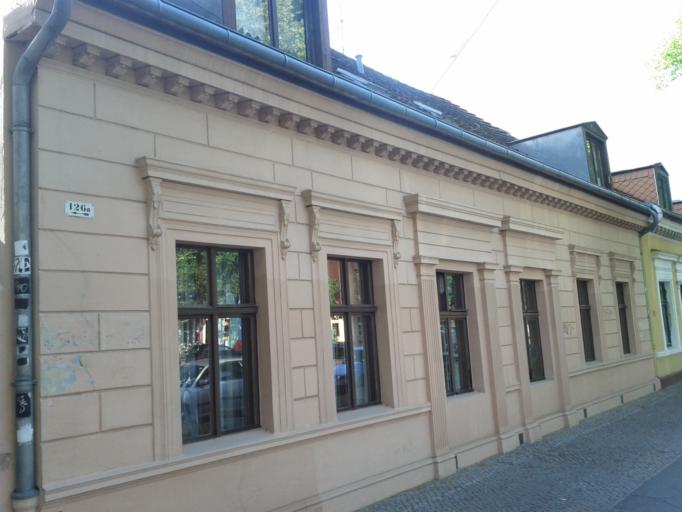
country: DE
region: Berlin
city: Friedrichshagen
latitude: 52.4484
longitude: 13.6243
